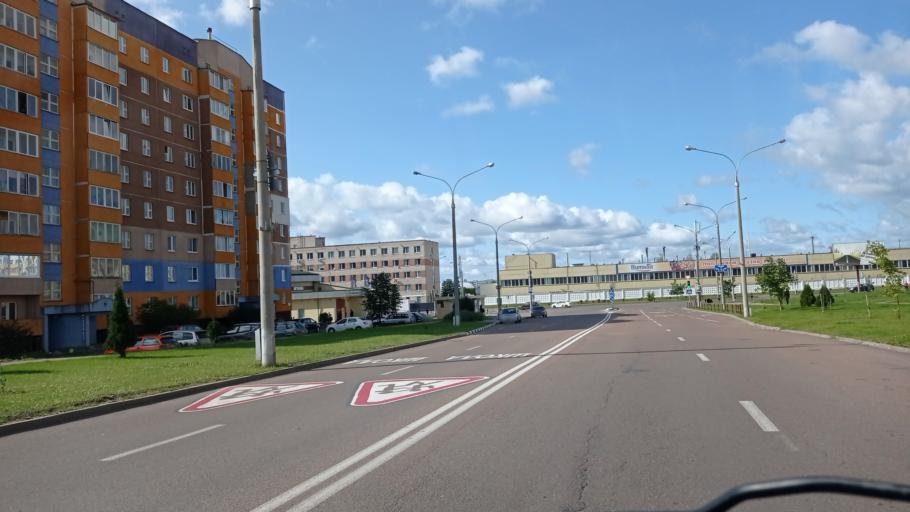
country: BY
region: Vitebsk
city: Vitebsk
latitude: 55.1700
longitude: 30.2592
